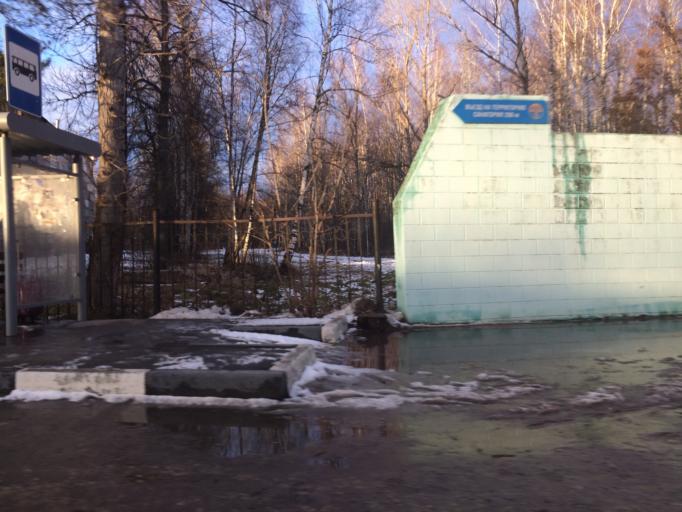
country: RU
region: Tula
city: Cherepet'
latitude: 54.1113
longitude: 36.3404
